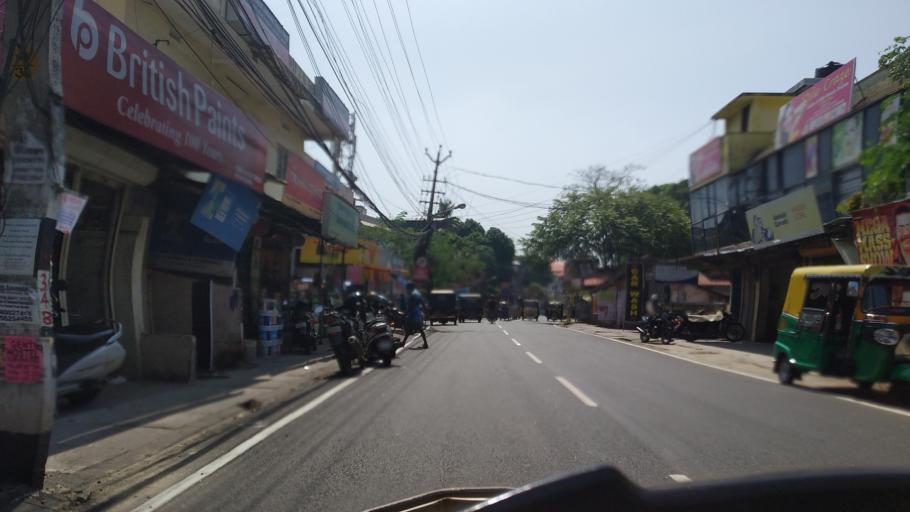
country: IN
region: Kerala
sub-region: Ernakulam
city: Elur
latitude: 9.9976
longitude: 76.3078
